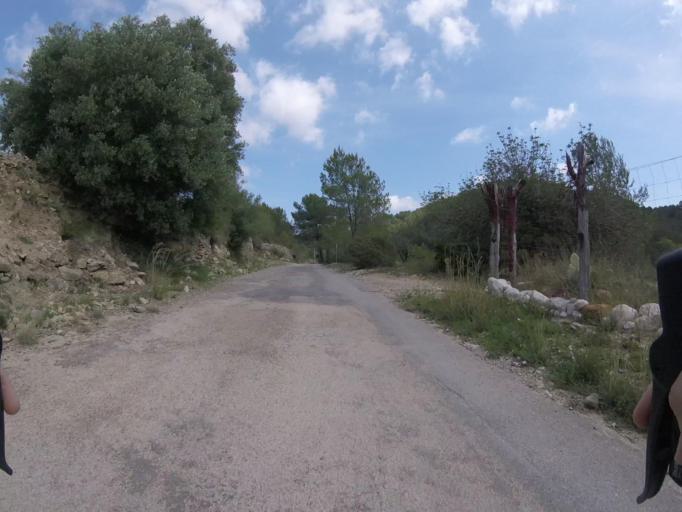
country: ES
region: Valencia
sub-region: Provincia de Castello
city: Cabanes
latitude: 40.1148
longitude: 0.0474
